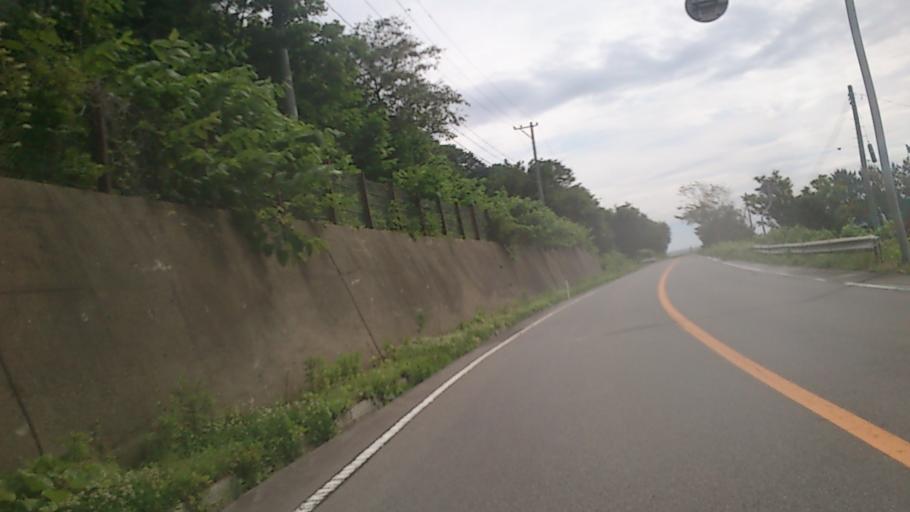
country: JP
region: Akita
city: Noshiromachi
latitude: 40.4489
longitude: 139.9428
